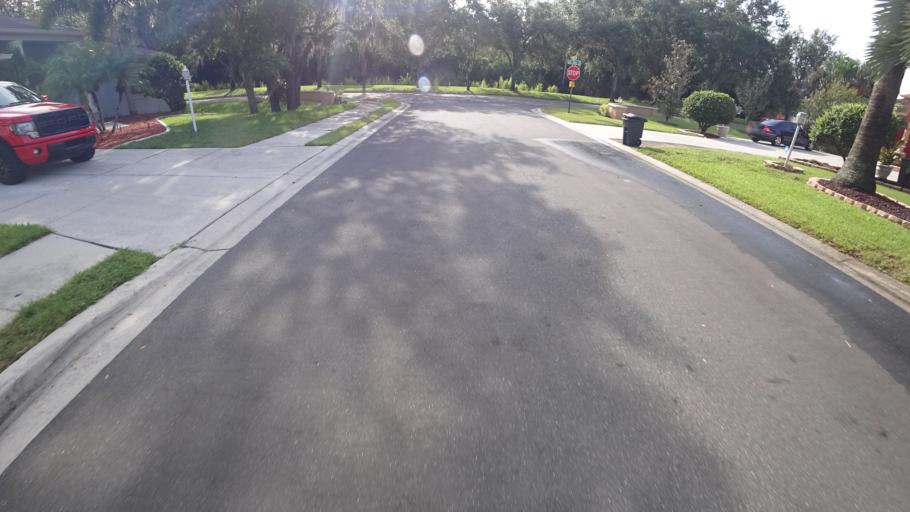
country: US
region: Florida
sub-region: Manatee County
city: Ellenton
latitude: 27.5403
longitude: -82.5038
